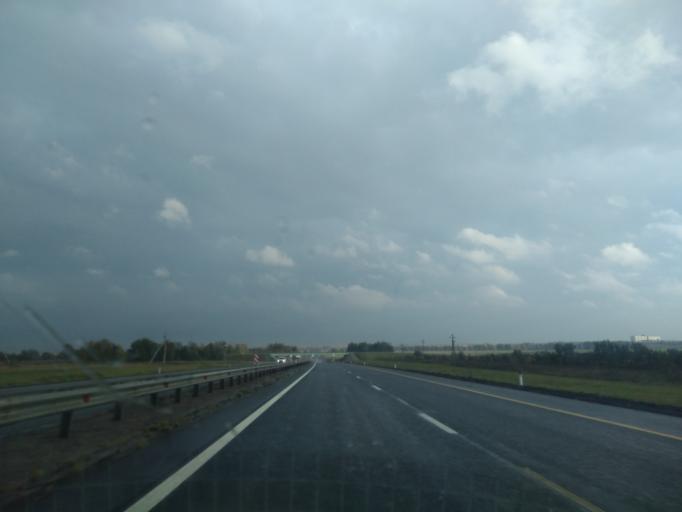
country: RU
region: Lipetsk
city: Yelets
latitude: 52.5829
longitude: 38.6859
